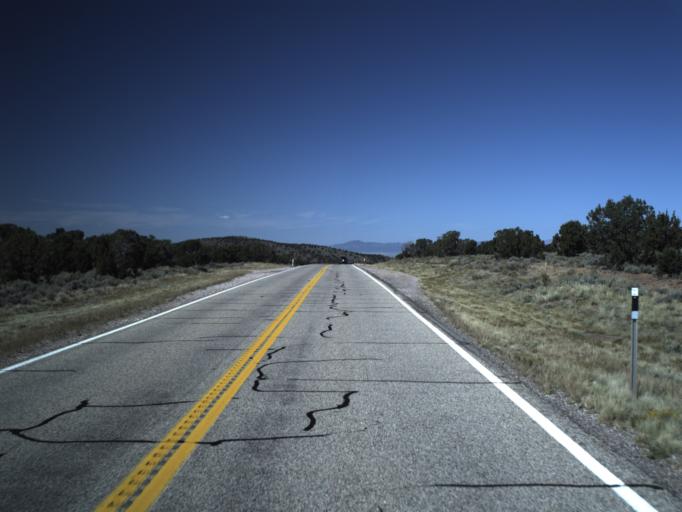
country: US
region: Utah
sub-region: Washington County
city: Enterprise
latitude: 37.6627
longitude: -113.4659
